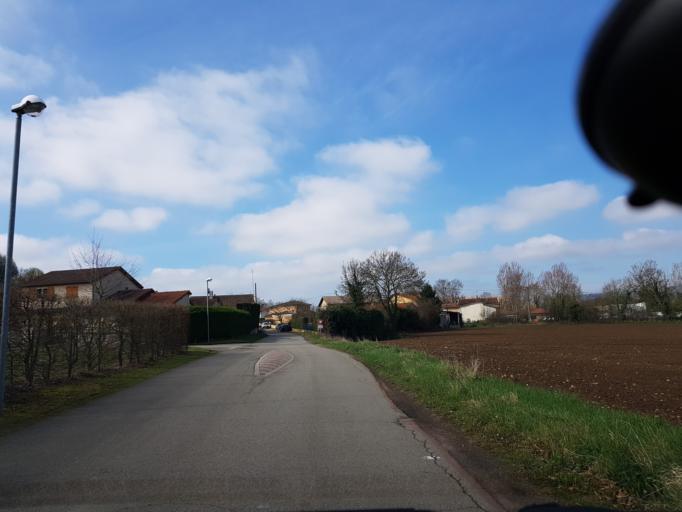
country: FR
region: Rhone-Alpes
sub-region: Departement de l'Ain
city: Trevoux
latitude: 45.9512
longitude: 4.7606
